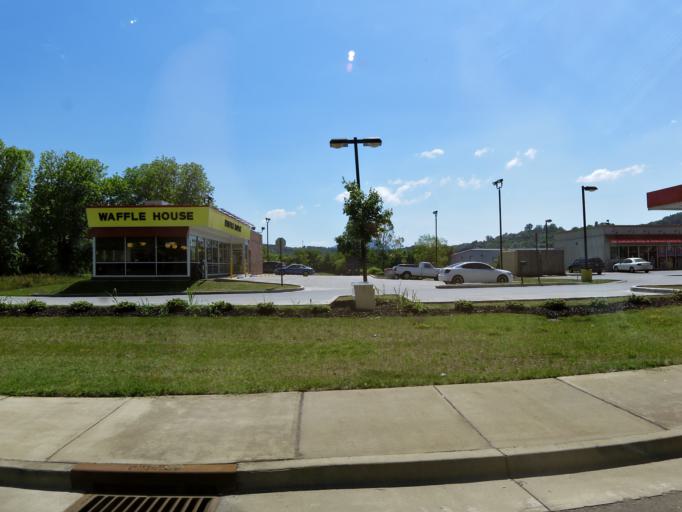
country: US
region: Tennessee
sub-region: Sevier County
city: Sevierville
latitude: 35.8720
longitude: -83.5681
